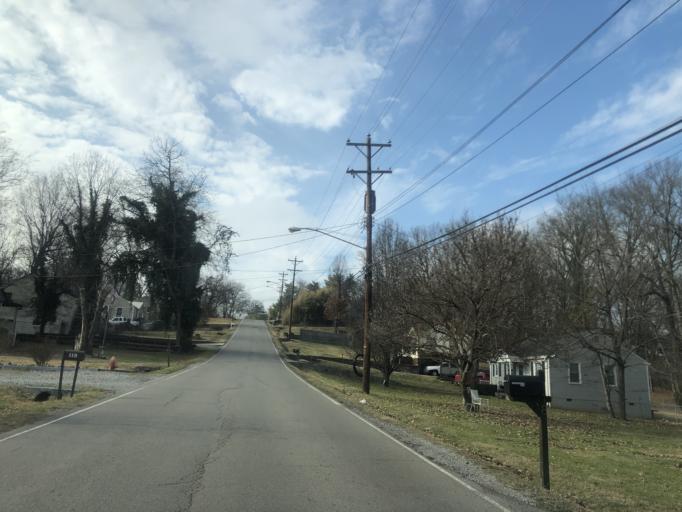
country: US
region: Tennessee
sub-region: Davidson County
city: Oak Hill
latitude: 36.1072
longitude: -86.7226
